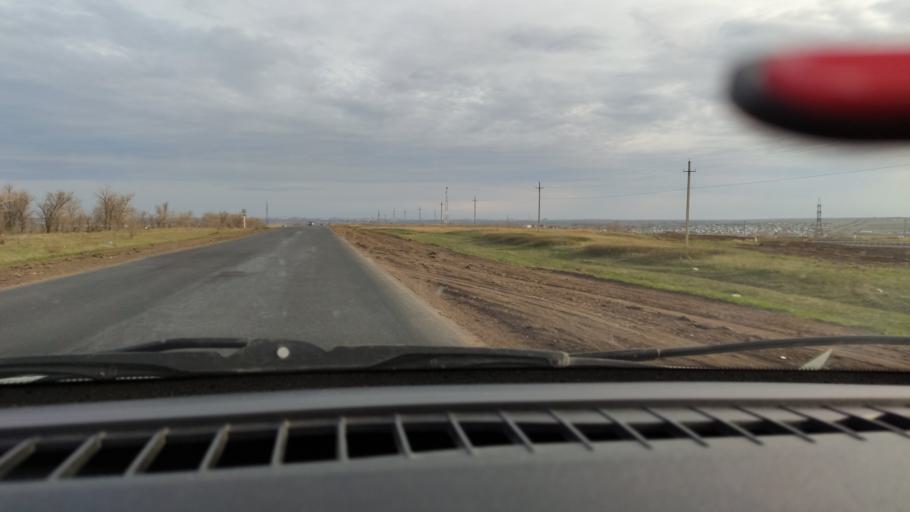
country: RU
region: Orenburg
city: Tatarskaya Kargala
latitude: 51.9665
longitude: 55.1850
